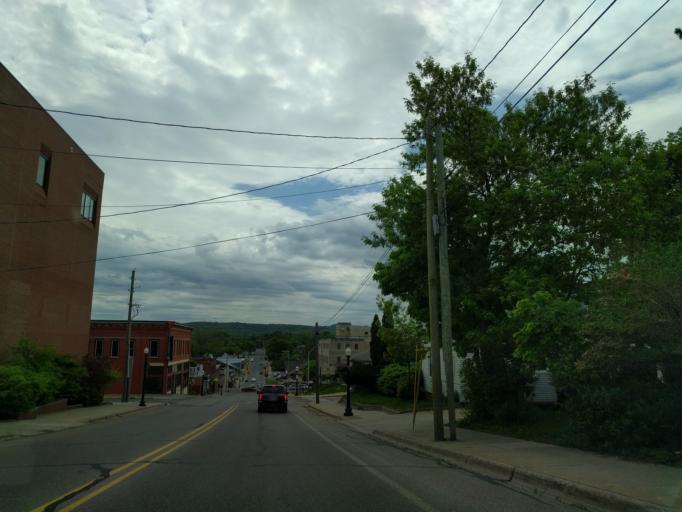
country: US
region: Michigan
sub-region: Marquette County
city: Marquette
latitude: 46.5451
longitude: -87.3949
